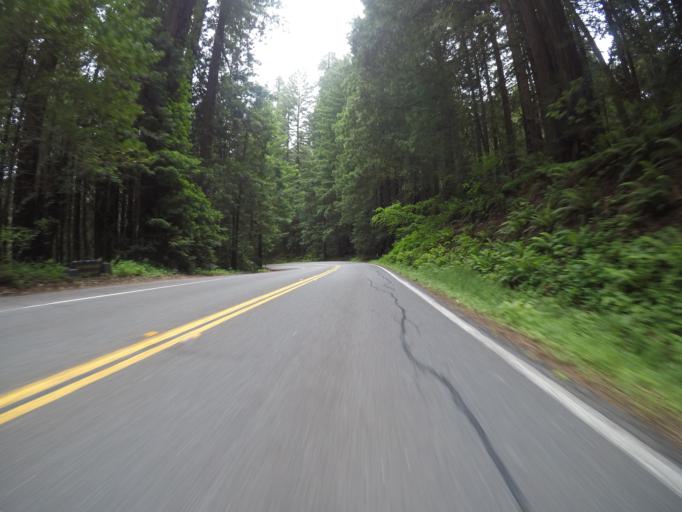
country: US
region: California
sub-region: Humboldt County
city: Rio Dell
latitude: 40.3965
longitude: -123.9362
